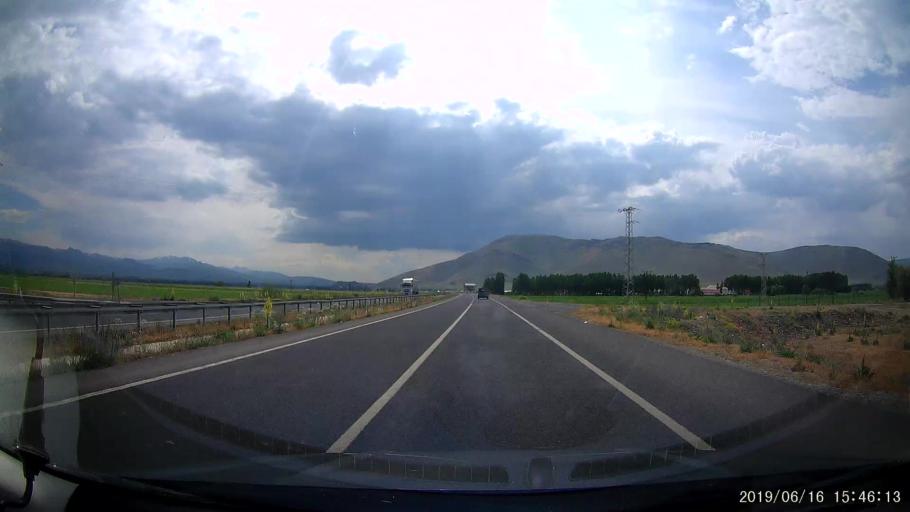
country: TR
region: Erzurum
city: Pasinler
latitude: 39.9900
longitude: 41.7498
